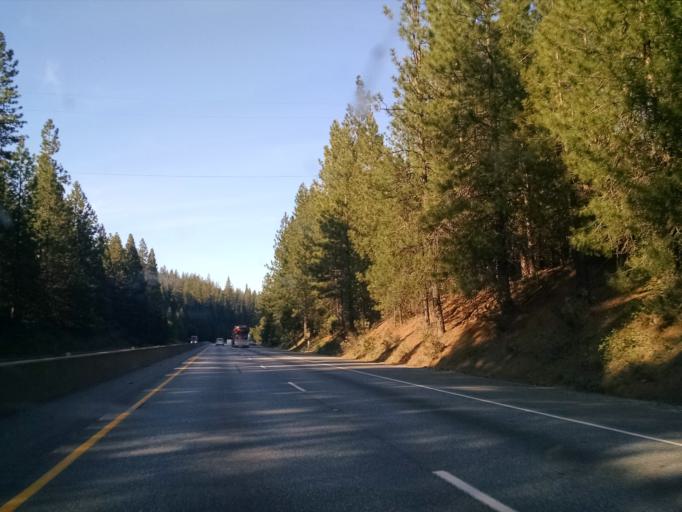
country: US
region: California
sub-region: Siskiyou County
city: Dunsmuir
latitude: 41.0589
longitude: -122.3719
